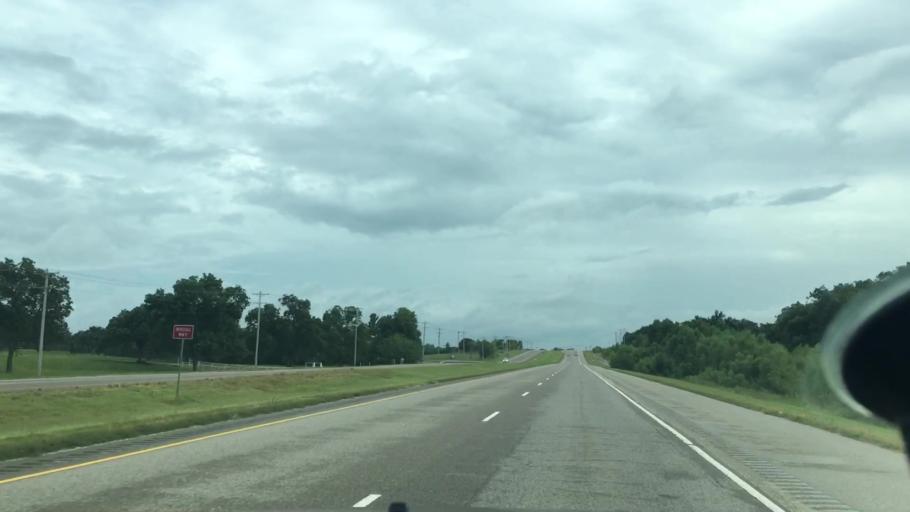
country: US
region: Oklahoma
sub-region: Seminole County
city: Seminole
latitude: 35.3403
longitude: -96.6718
